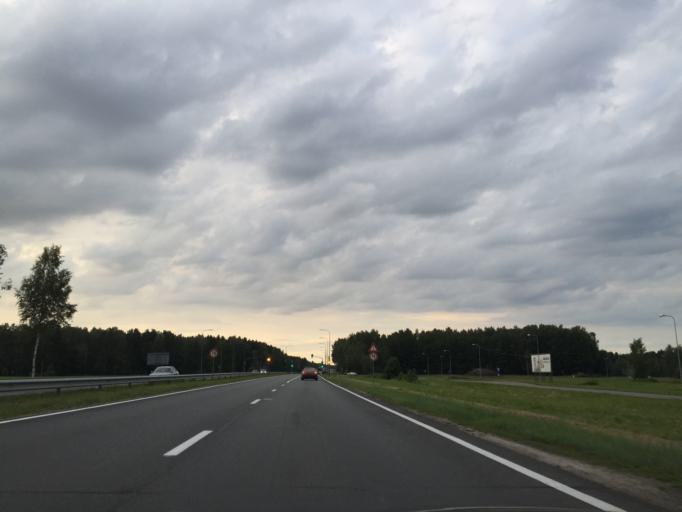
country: LV
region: Babite
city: Pinki
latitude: 56.9430
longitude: 23.9217
